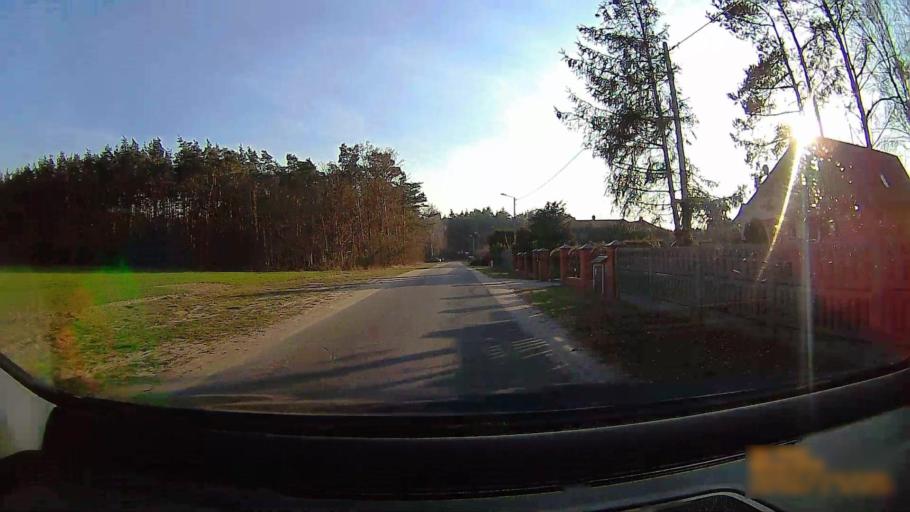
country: PL
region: Greater Poland Voivodeship
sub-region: Konin
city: Konin
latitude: 52.1774
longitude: 18.3005
